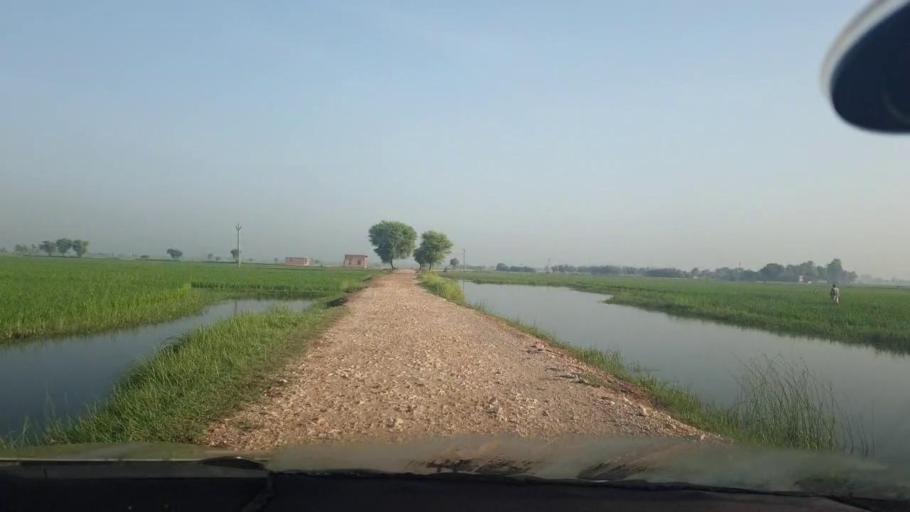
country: PK
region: Sindh
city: Kambar
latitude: 27.6309
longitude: 68.0171
